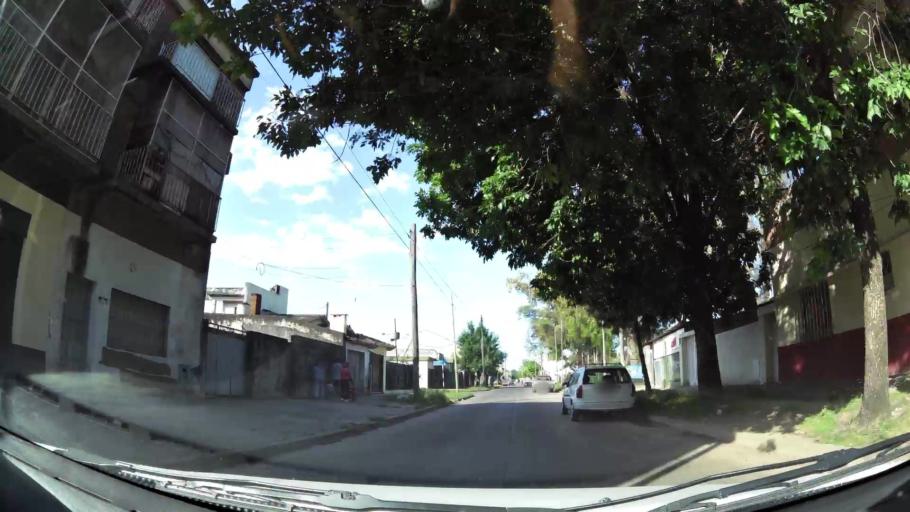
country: AR
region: Buenos Aires
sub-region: Partido de General San Martin
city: General San Martin
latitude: -34.5507
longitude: -58.5418
